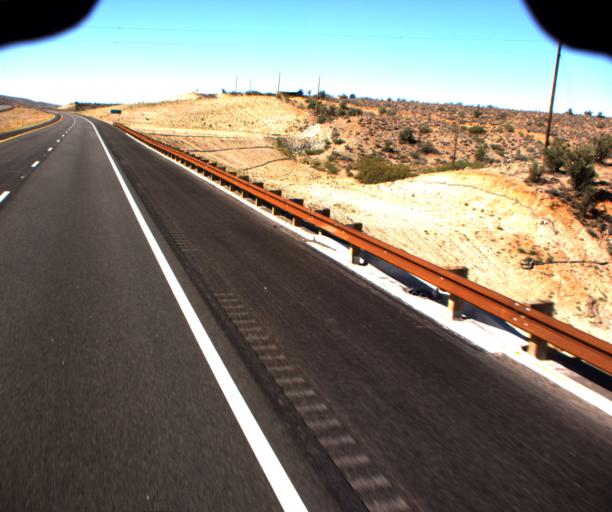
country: US
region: Arizona
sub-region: Mohave County
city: Kingman
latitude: 35.0091
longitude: -113.6646
